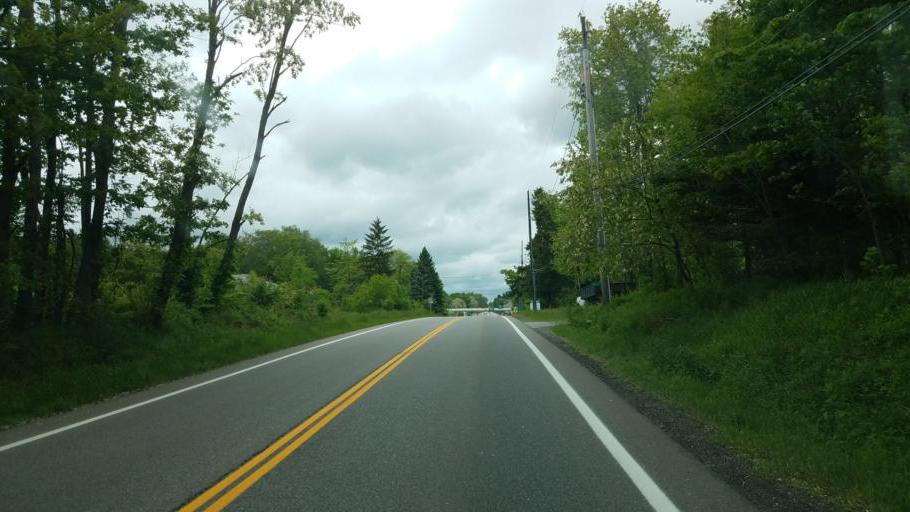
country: US
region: Ohio
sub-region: Portage County
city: Mantua
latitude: 41.3796
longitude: -81.2176
